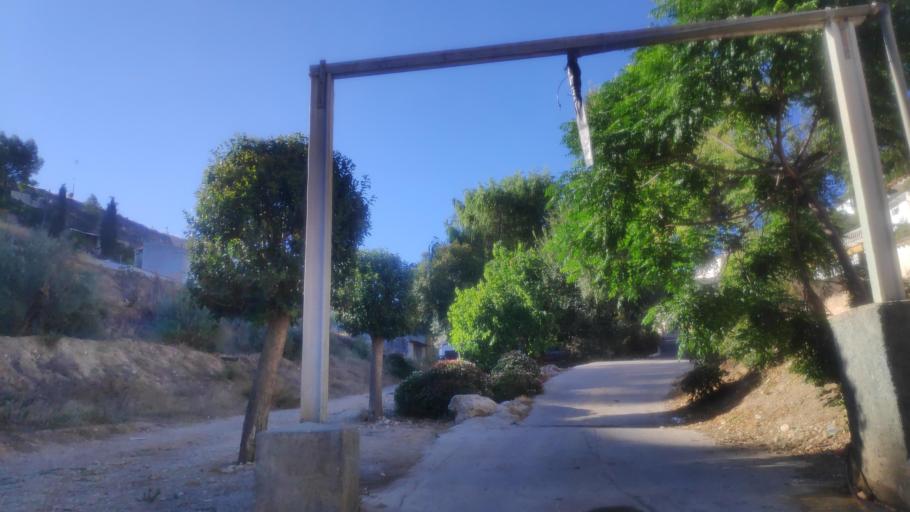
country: ES
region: Andalusia
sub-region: Provincia de Jaen
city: Hinojares
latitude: 37.6757
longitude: -2.9732
